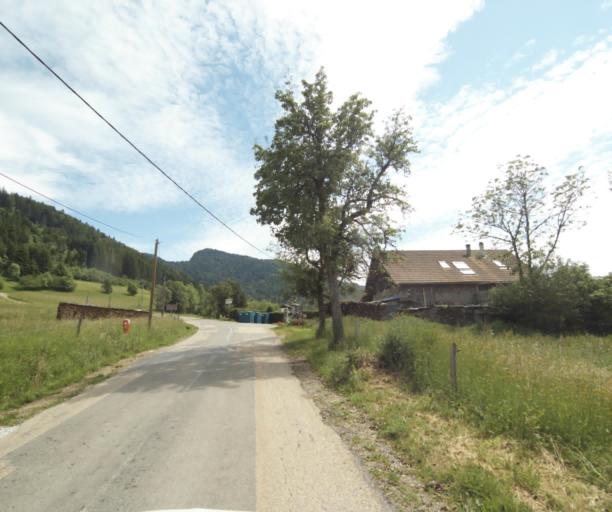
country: FR
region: Rhone-Alpes
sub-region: Departement de la Haute-Savoie
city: Perrignier
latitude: 46.2952
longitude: 6.4741
